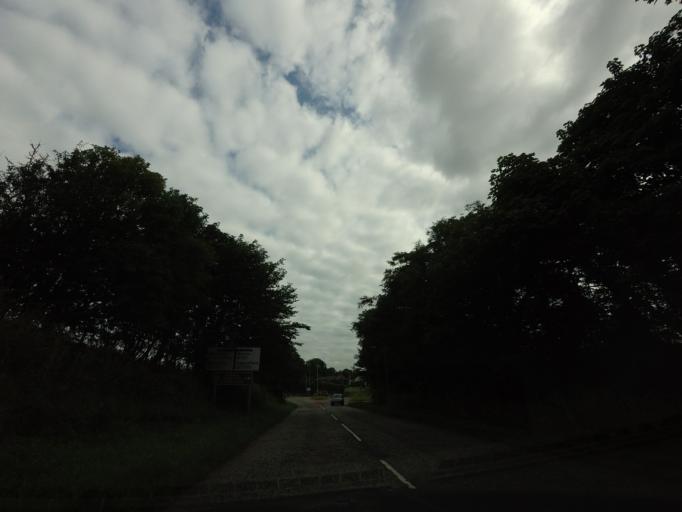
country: GB
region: Scotland
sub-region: Dumfries and Galloway
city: Annan
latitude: 54.9891
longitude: -3.2730
